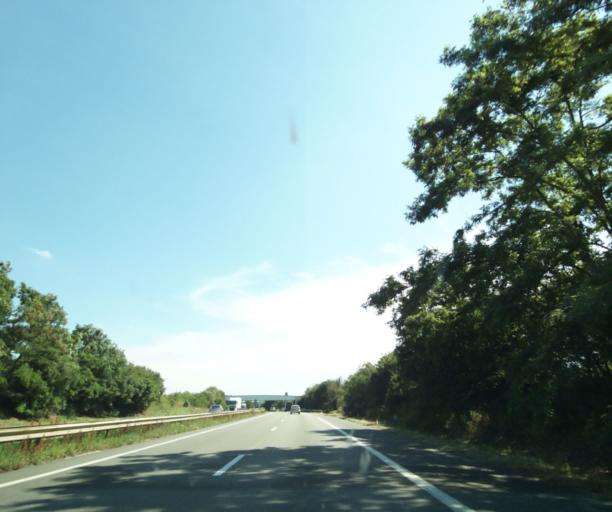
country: FR
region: Lorraine
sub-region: Departement de Meurthe-et-Moselle
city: Dommartin-les-Toul
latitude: 48.6595
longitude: 5.9087
